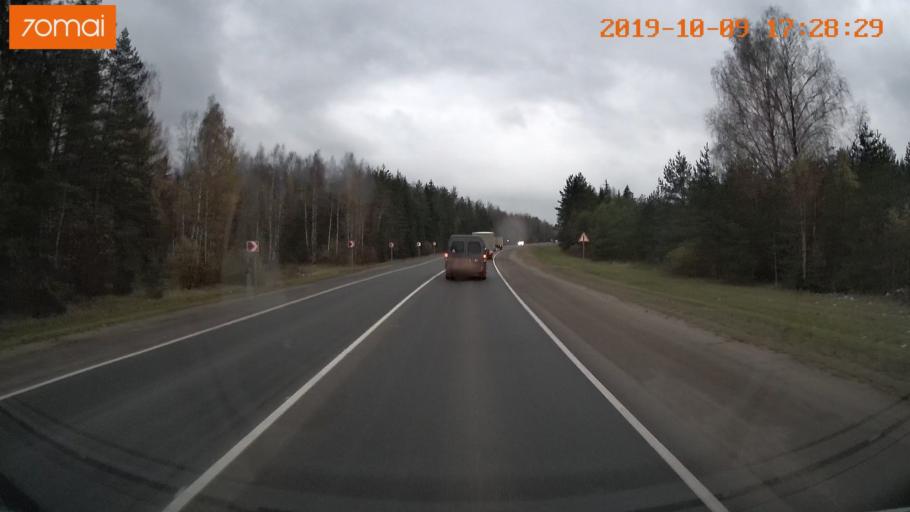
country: RU
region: Ivanovo
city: Furmanov
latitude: 57.1576
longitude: 41.0681
